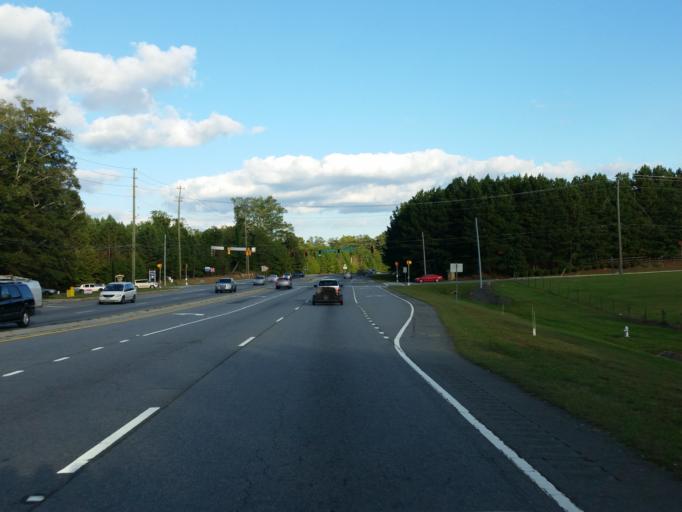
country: US
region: Georgia
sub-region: Cobb County
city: Powder Springs
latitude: 33.9022
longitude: -84.6684
